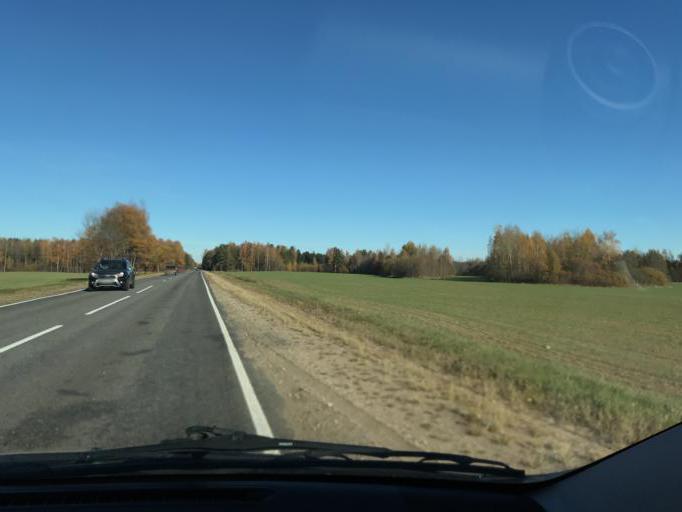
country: BY
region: Vitebsk
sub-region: Ushatski Rayon
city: Ushachy
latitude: 55.0877
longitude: 28.7562
